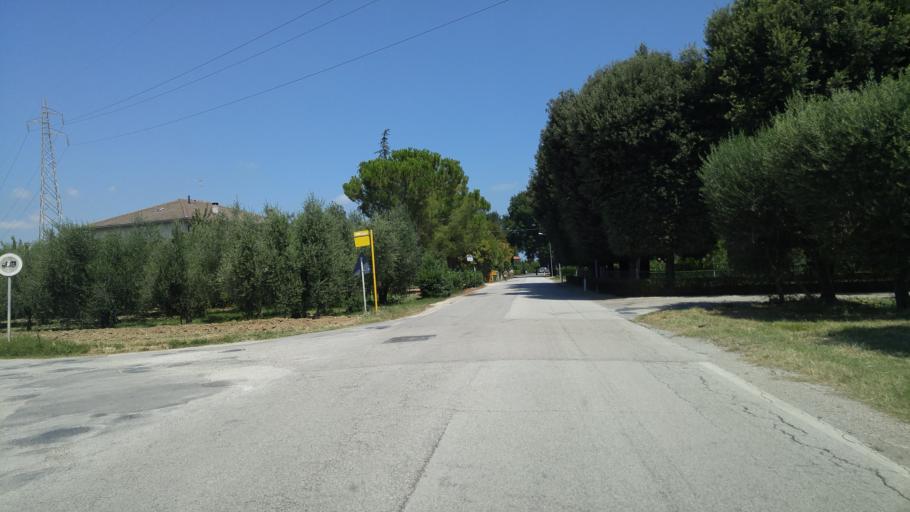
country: IT
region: The Marches
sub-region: Provincia di Pesaro e Urbino
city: Bellocchi
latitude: 43.7997
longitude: 13.0033
